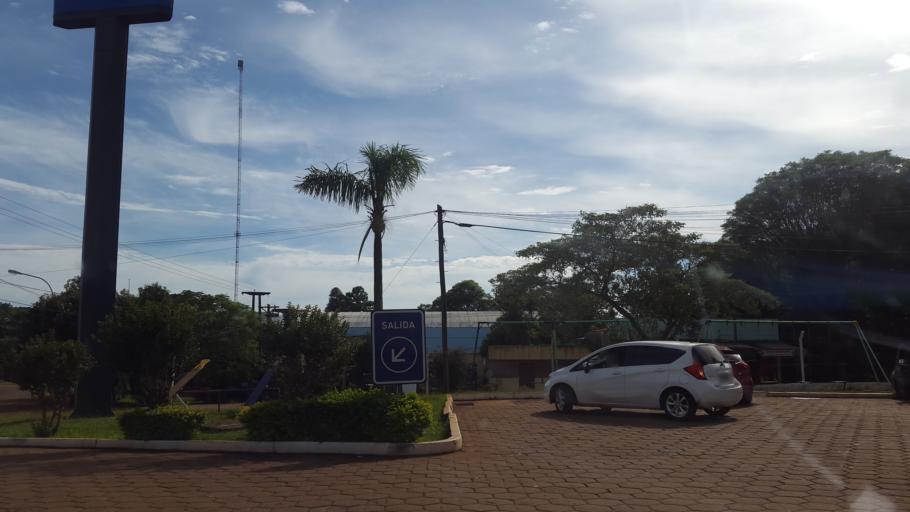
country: AR
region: Misiones
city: Bernardo de Irigoyen
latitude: -26.2614
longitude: -53.6483
